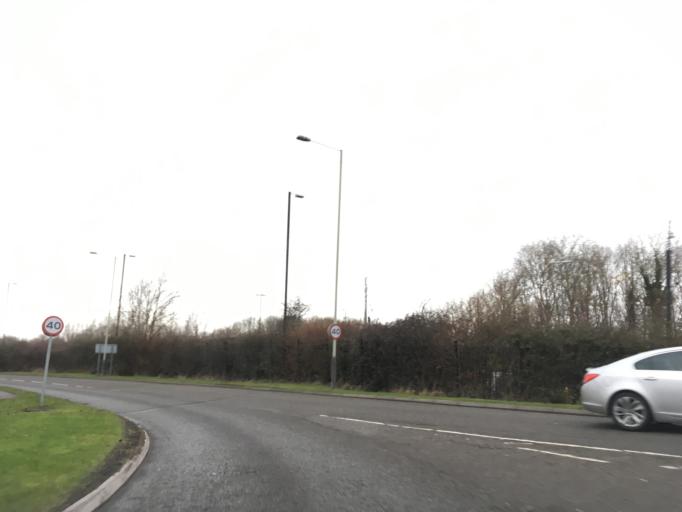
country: GB
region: England
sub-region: Gloucestershire
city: Uckington
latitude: 51.8929
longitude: -2.1314
